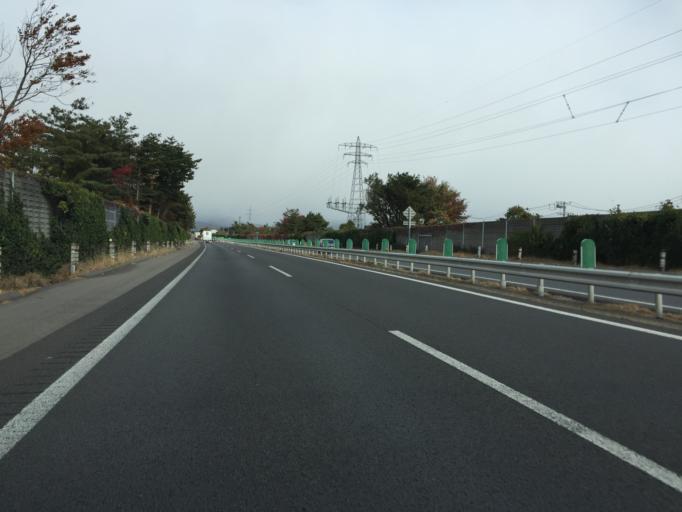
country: JP
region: Fukushima
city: Fukushima-shi
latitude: 37.7705
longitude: 140.4126
